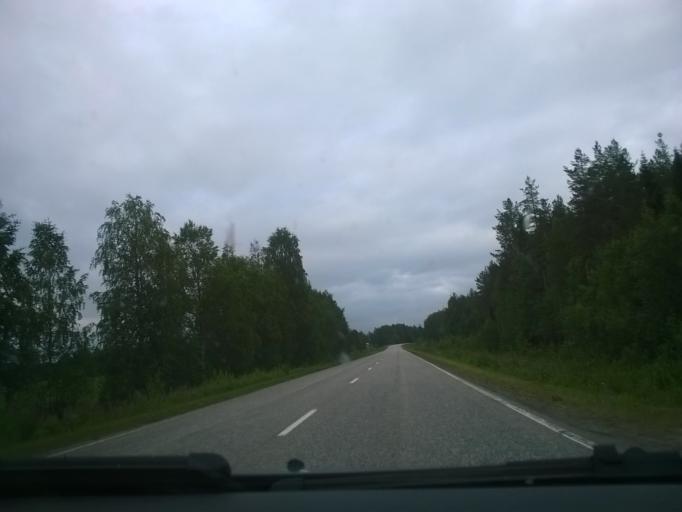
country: FI
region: Kainuu
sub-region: Kehys-Kainuu
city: Kuhmo
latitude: 64.1447
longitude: 29.4268
